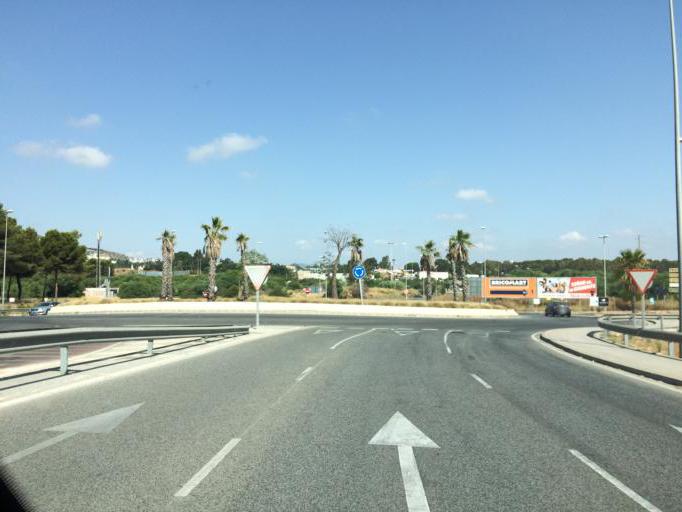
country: ES
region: Andalusia
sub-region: Provincia de Malaga
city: Torremolinos
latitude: 36.6549
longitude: -4.4818
